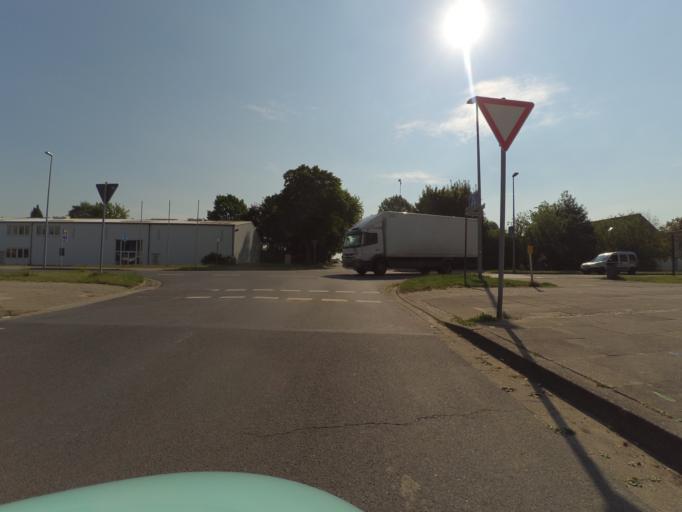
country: DE
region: Lower Saxony
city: Burgdorf
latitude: 52.4423
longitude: 10.0261
